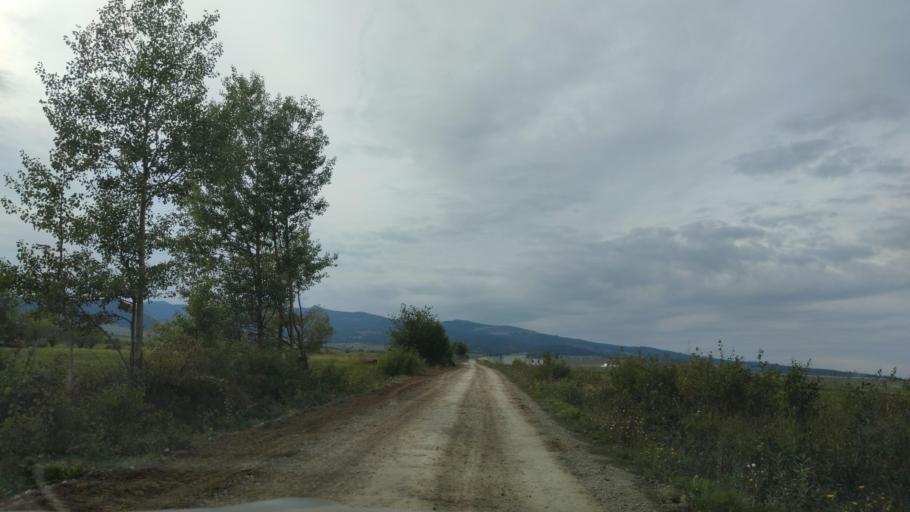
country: RO
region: Harghita
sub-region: Comuna Subcetate
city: Subcetate
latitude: 46.8168
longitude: 25.4155
